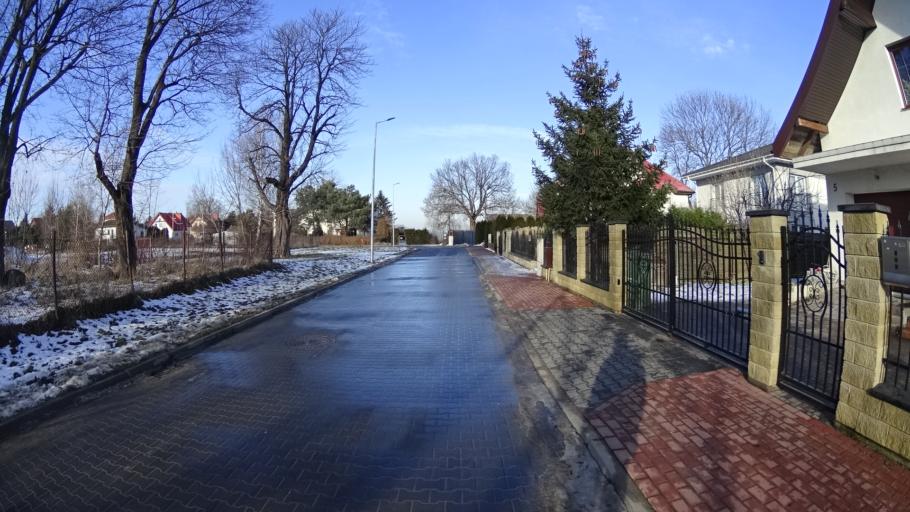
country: PL
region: Masovian Voivodeship
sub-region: Powiat warszawski zachodni
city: Babice
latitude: 52.2271
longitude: 20.8691
